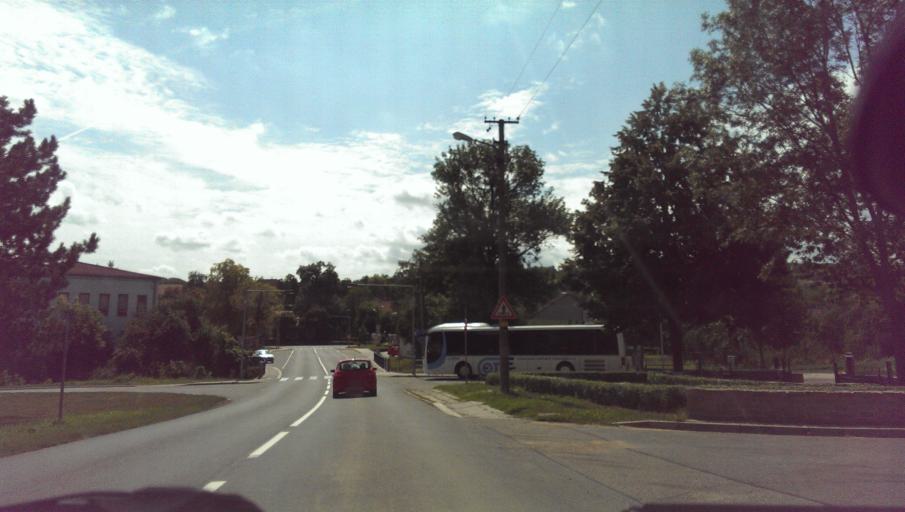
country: CZ
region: Zlin
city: Bilovice
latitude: 49.1004
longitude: 17.5476
